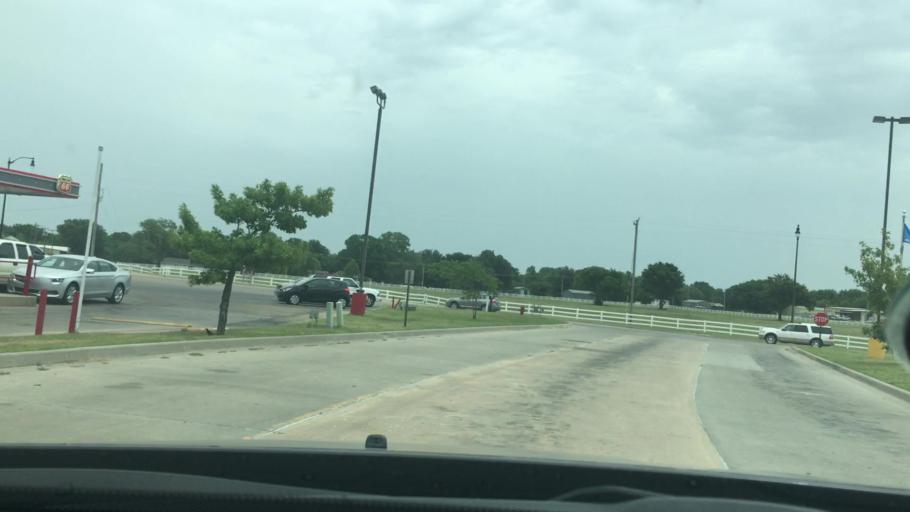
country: US
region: Oklahoma
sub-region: Pontotoc County
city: Ada
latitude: 34.7732
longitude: -96.6985
